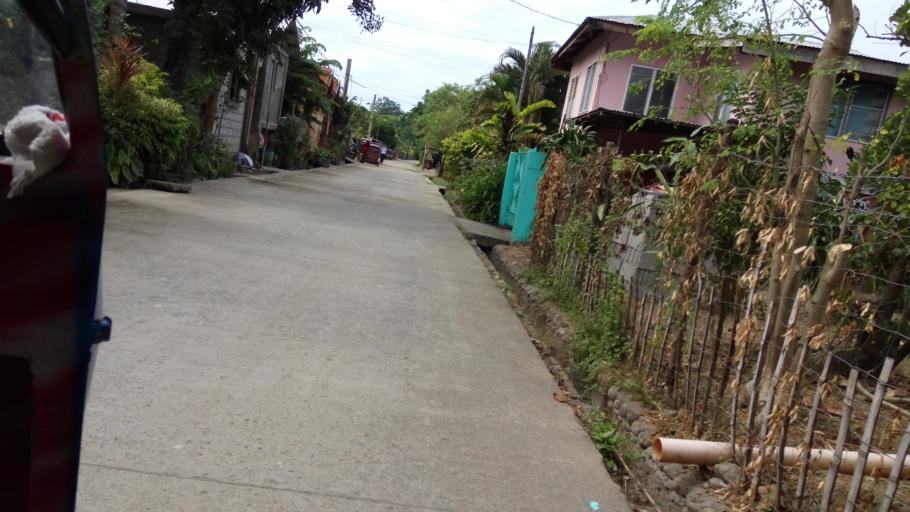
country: PH
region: Ilocos
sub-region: Province of La Union
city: Aringay
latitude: 16.3932
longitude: 120.3525
